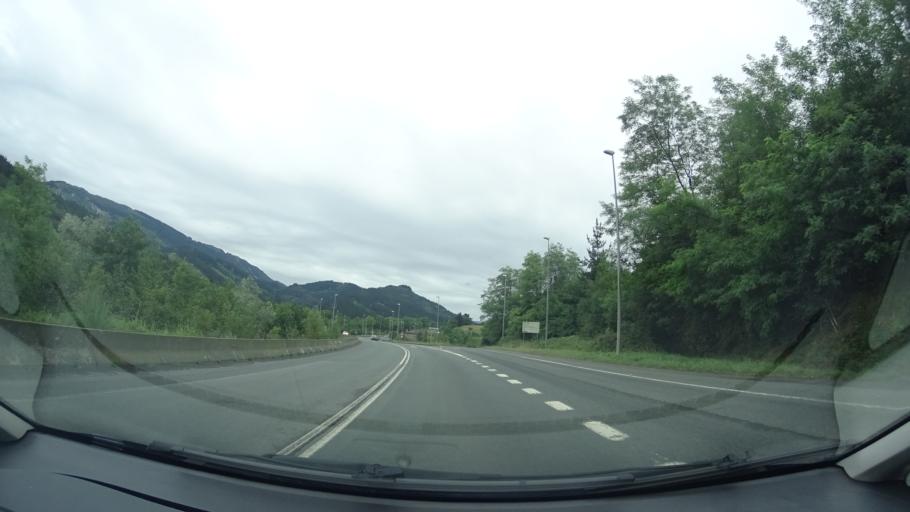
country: ES
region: Basque Country
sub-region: Bizkaia
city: Amorebieta
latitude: 43.1901
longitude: -2.7761
